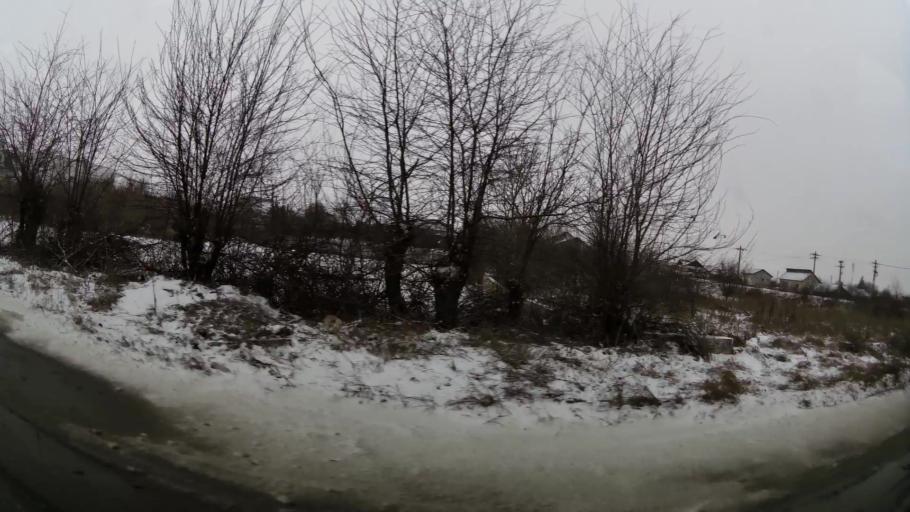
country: RO
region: Dambovita
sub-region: Comuna Ulmi
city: Ulmi
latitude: 44.9038
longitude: 25.4967
